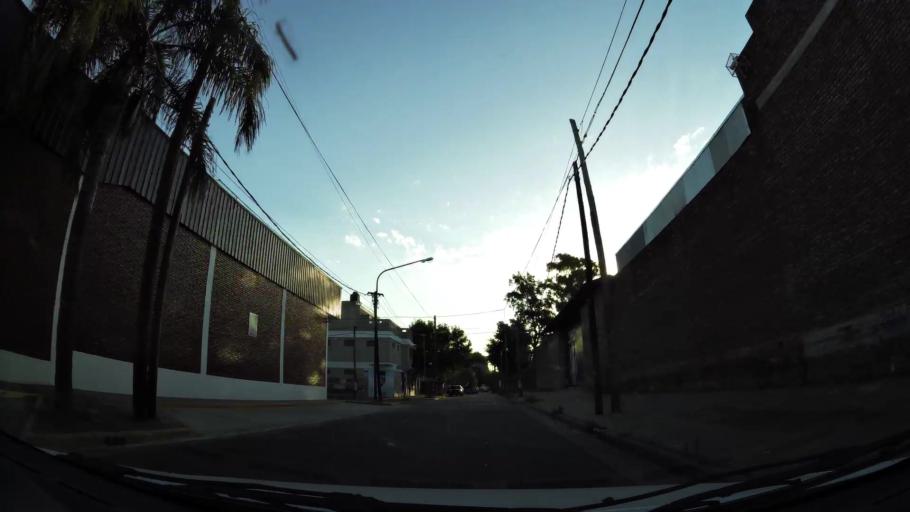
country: AR
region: Buenos Aires
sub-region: Partido de General San Martin
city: General San Martin
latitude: -34.5649
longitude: -58.5231
